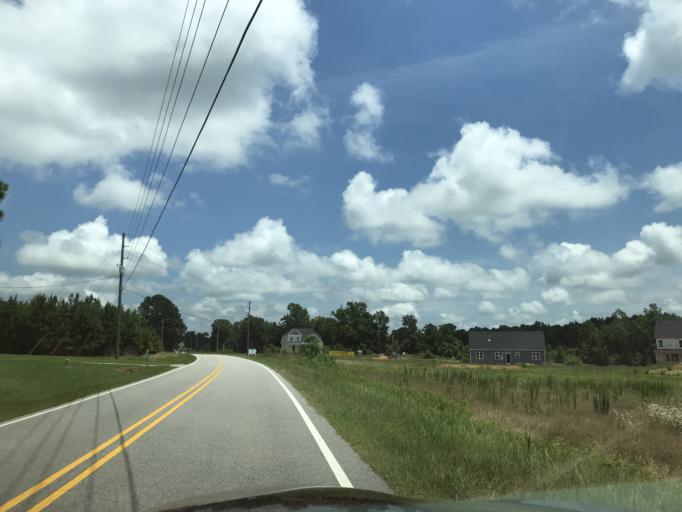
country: US
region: North Carolina
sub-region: Wake County
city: Rolesville
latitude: 35.9507
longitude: -78.3792
